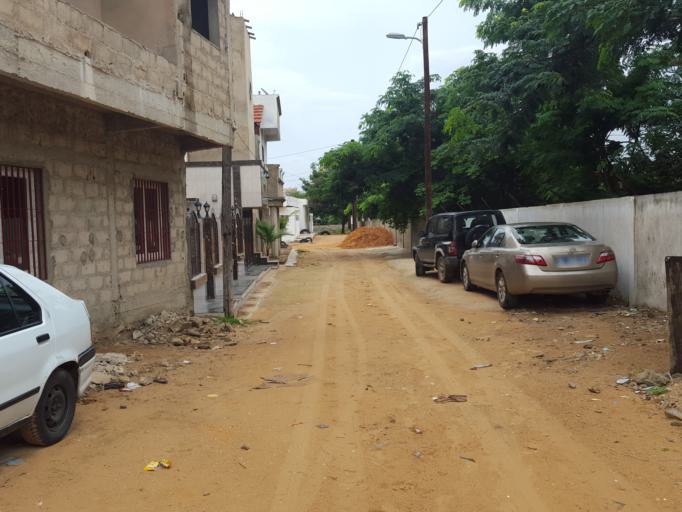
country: SN
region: Dakar
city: Grand Dakar
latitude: 14.7333
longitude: -17.4656
